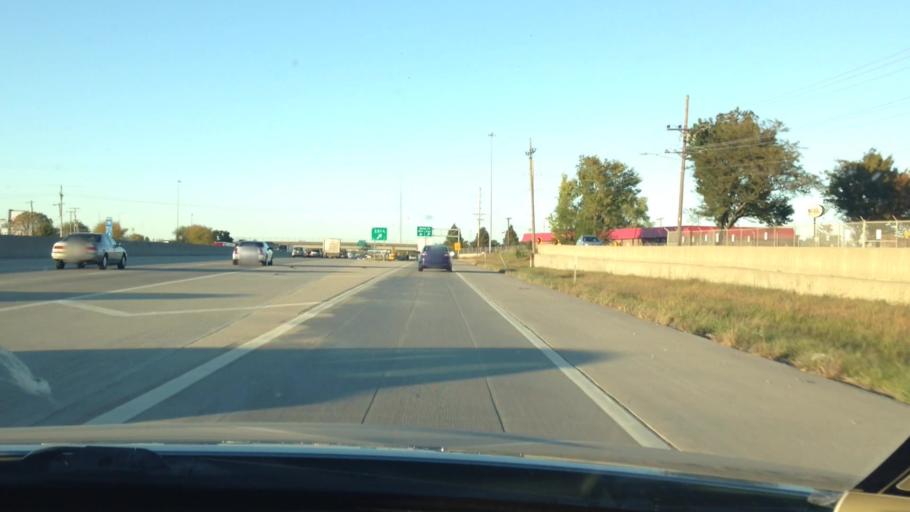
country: US
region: Kansas
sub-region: Johnson County
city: Olathe
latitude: 38.8801
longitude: -94.7922
